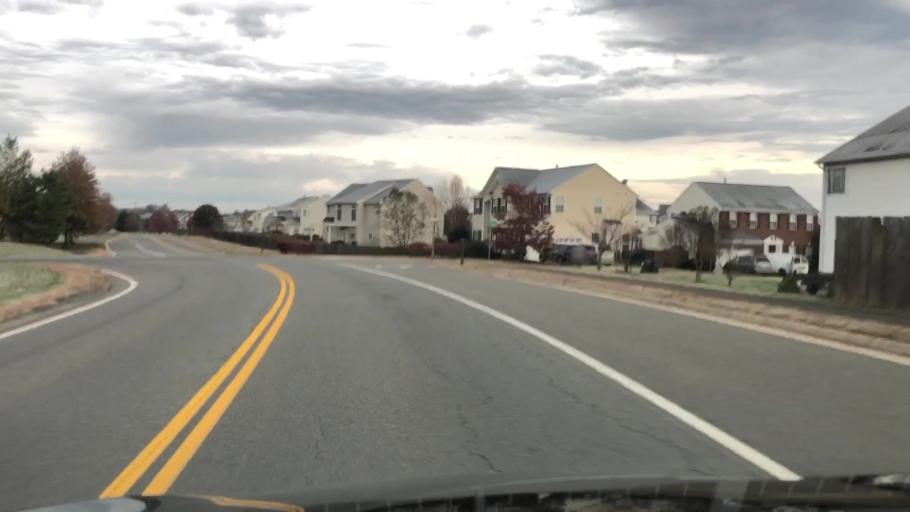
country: US
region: Virginia
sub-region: Fauquier County
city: Bealeton
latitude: 38.5792
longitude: -77.7599
